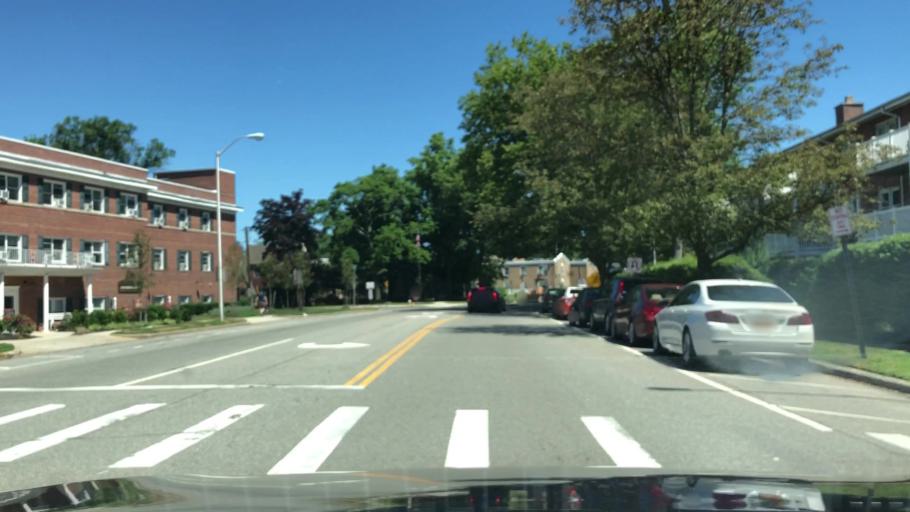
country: US
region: New York
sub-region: Nassau County
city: Rockville Centre
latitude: 40.6640
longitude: -73.6504
